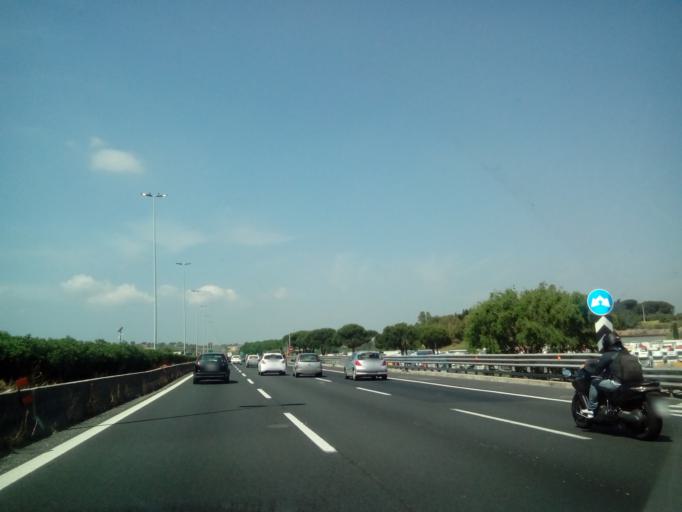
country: IT
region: Latium
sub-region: Citta metropolitana di Roma Capitale
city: Borgo Lotti
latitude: 41.7977
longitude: 12.5368
